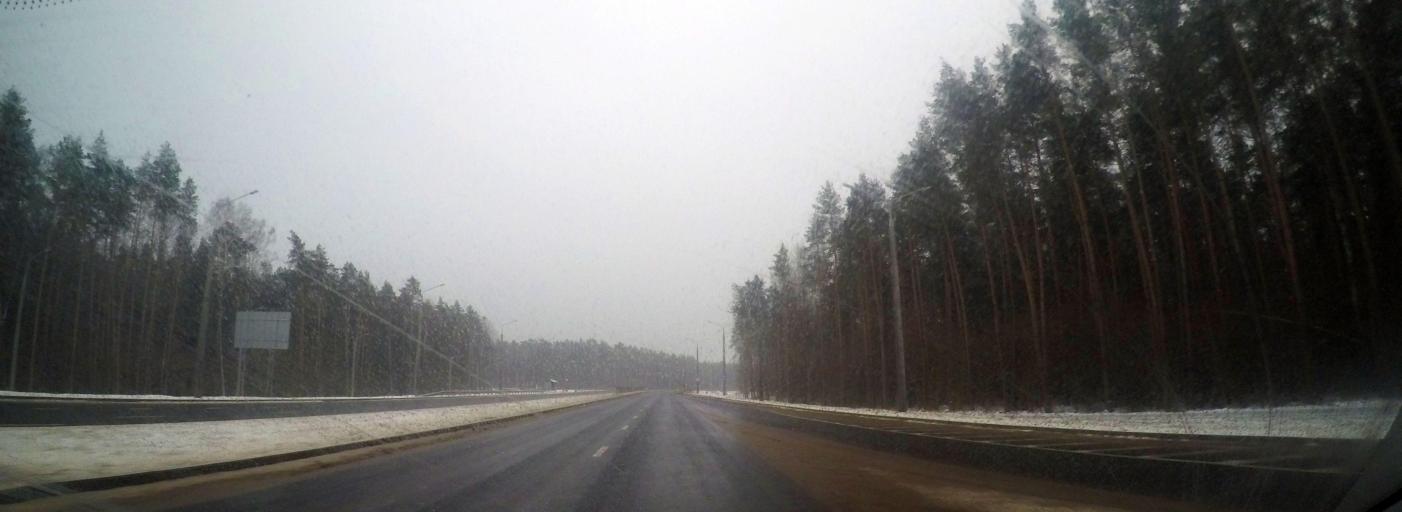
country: BY
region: Grodnenskaya
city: Hrodna
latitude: 53.6354
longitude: 23.8819
